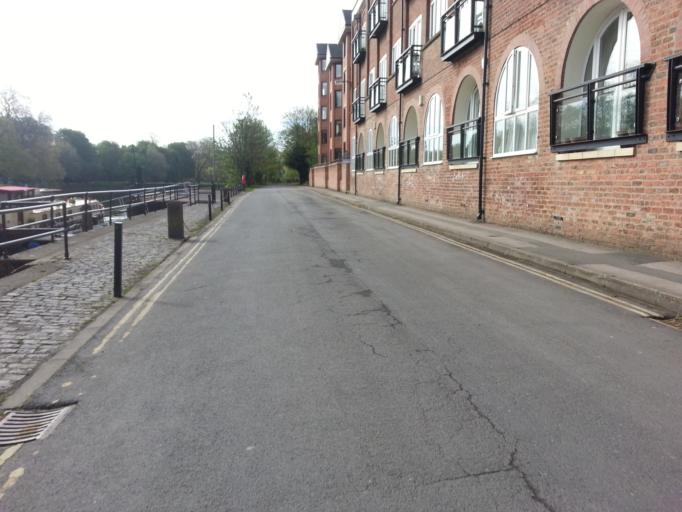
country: GB
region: England
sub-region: City of York
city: York
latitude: 53.9525
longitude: -1.0803
